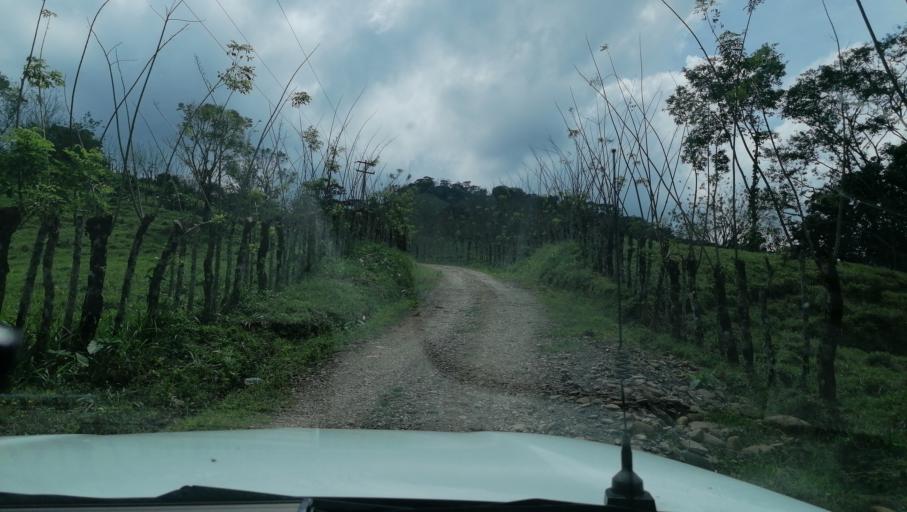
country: MX
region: Chiapas
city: Pichucalco
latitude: 17.4545
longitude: -93.2029
